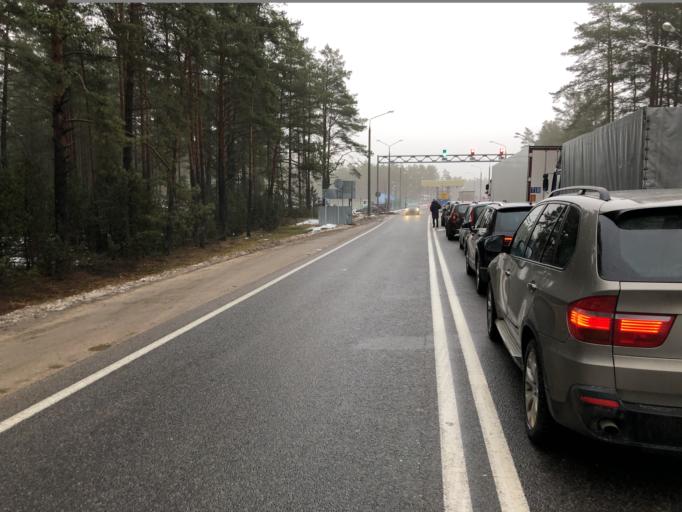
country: LT
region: Alytaus apskritis
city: Druskininkai
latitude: 53.9392
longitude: 23.9585
